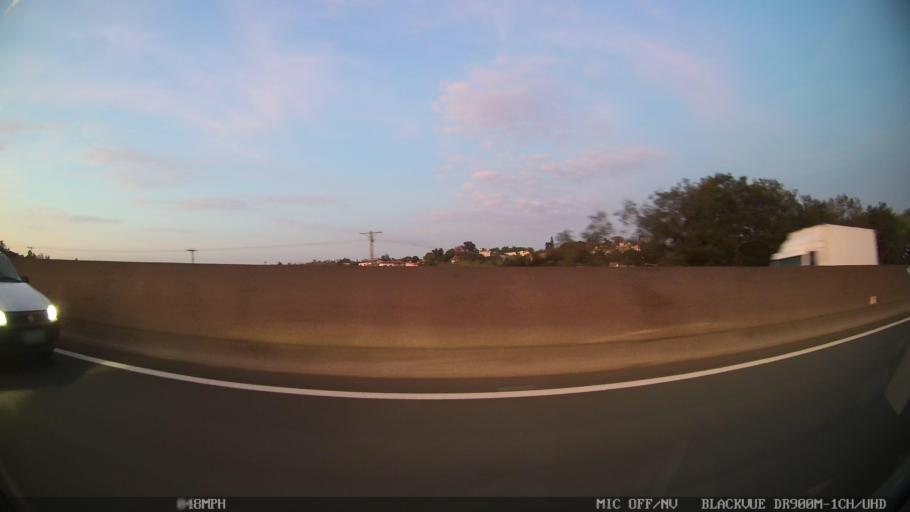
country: BR
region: Sao Paulo
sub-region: Vinhedo
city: Vinhedo
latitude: -23.0494
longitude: -47.0012
